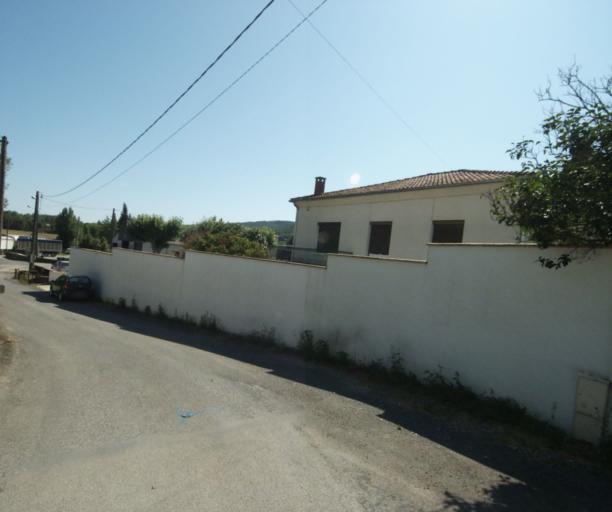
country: FR
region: Midi-Pyrenees
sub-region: Departement du Tarn
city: Soreze
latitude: 43.4460
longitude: 2.0521
